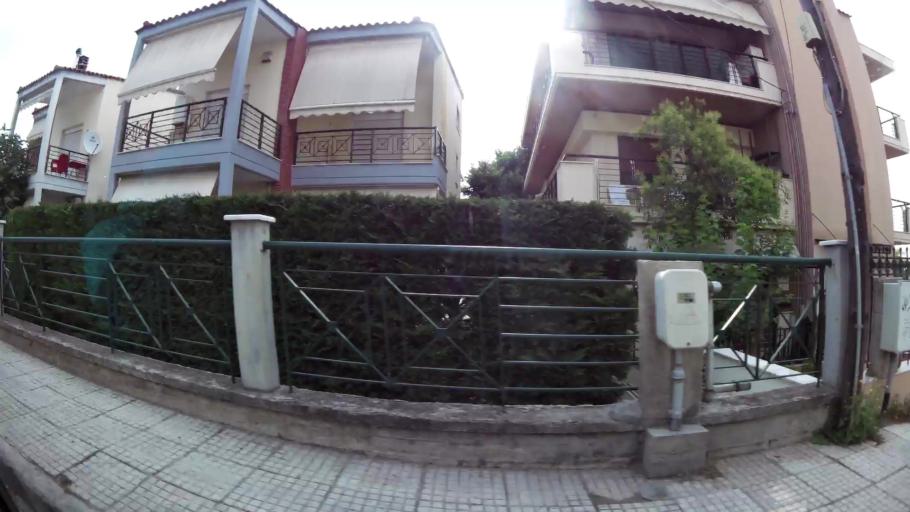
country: GR
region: Central Macedonia
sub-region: Nomos Thessalonikis
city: Panorama
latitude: 40.5879
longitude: 23.0354
